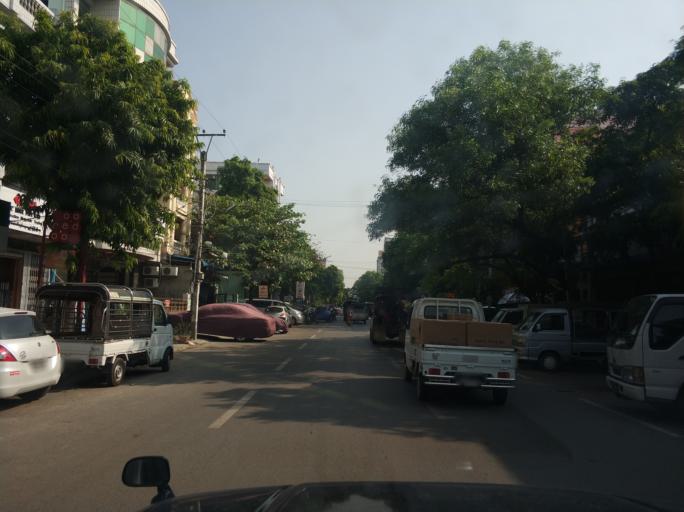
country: MM
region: Mandalay
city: Mandalay
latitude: 21.9796
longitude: 96.0793
